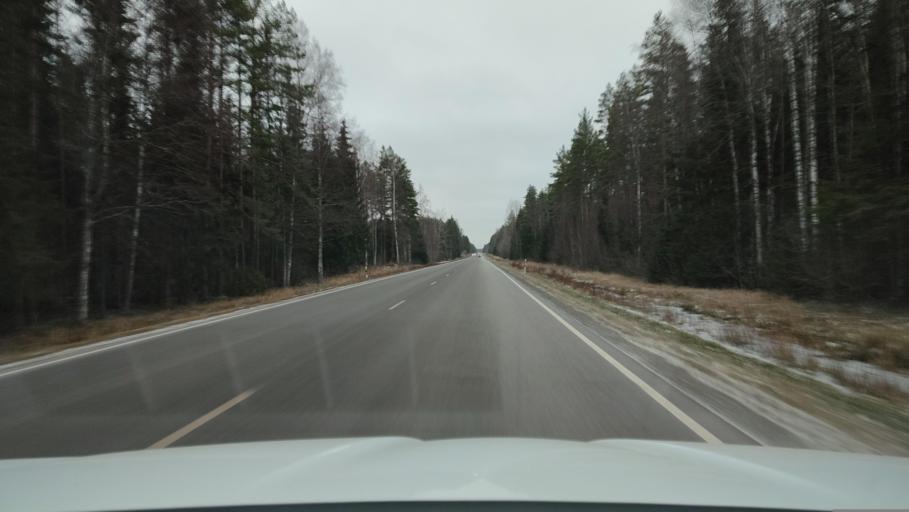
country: FI
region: Ostrobothnia
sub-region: Sydosterbotten
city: Naerpes
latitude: 62.5173
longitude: 21.4562
